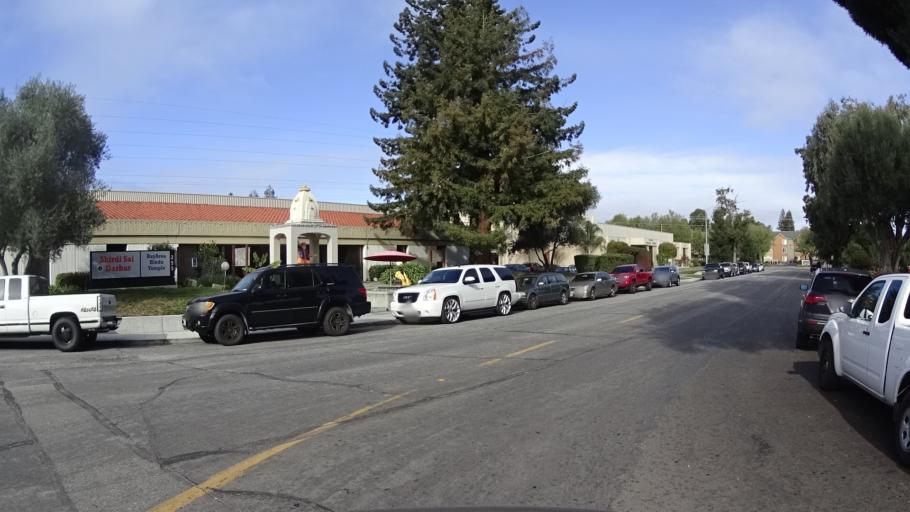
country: US
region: California
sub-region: Santa Clara County
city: Sunnyvale
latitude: 37.3797
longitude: -122.0141
